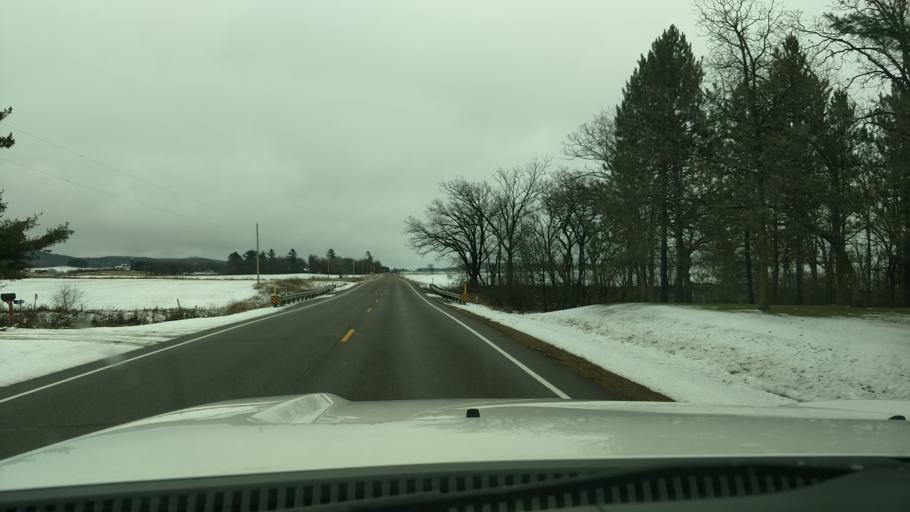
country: US
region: Wisconsin
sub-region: Dunn County
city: Colfax
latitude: 45.1427
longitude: -91.6960
